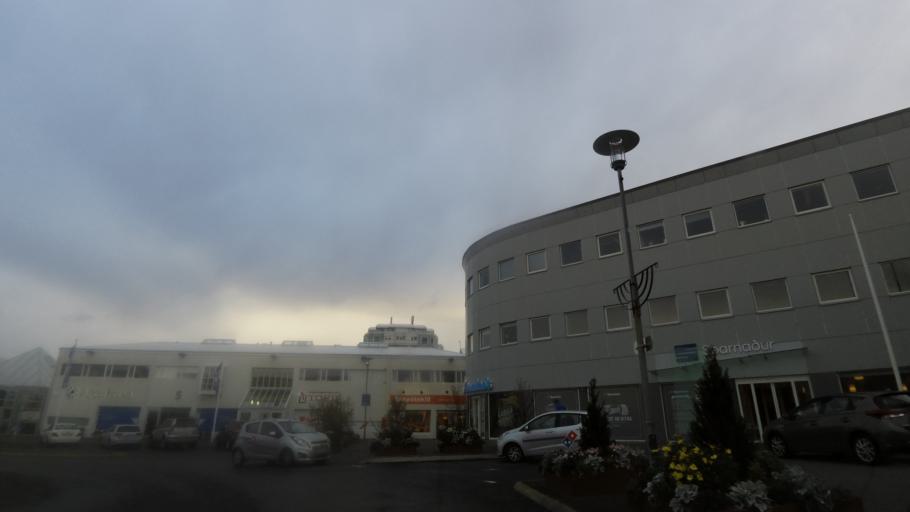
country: IS
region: Capital Region
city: Gardabaer
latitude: 64.0883
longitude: -21.9199
